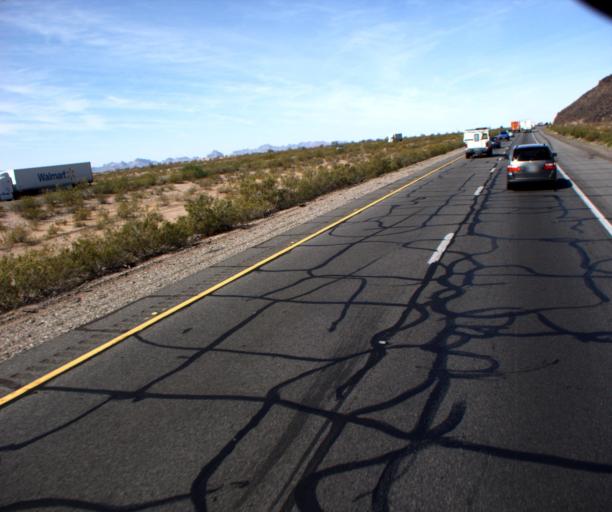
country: US
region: Arizona
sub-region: Maricopa County
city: Buckeye
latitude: 33.5271
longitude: -113.1064
